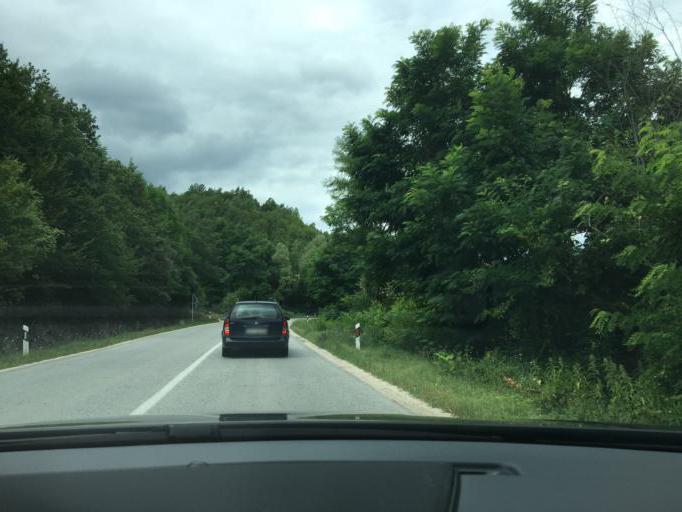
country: MK
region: Kratovo
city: Kratovo
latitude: 42.1744
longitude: 22.2220
